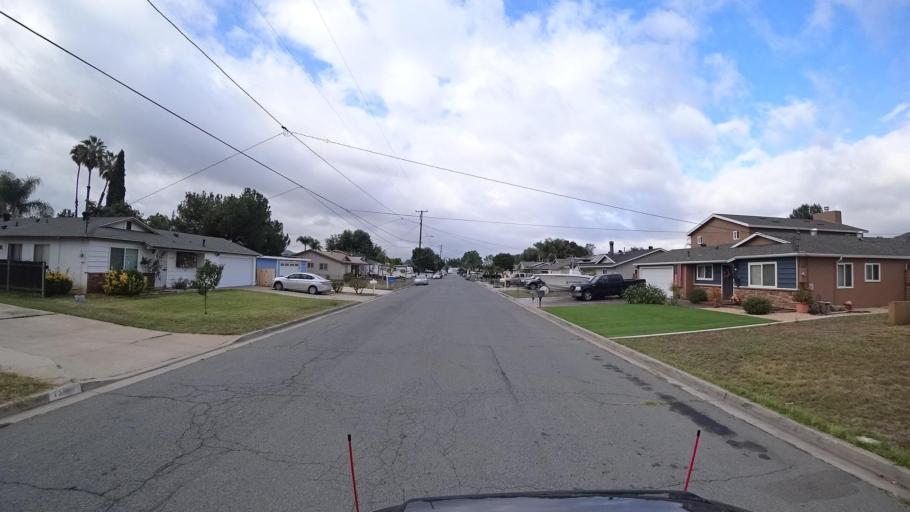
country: US
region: California
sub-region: San Diego County
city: Lakeside
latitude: 32.8606
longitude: -116.9098
